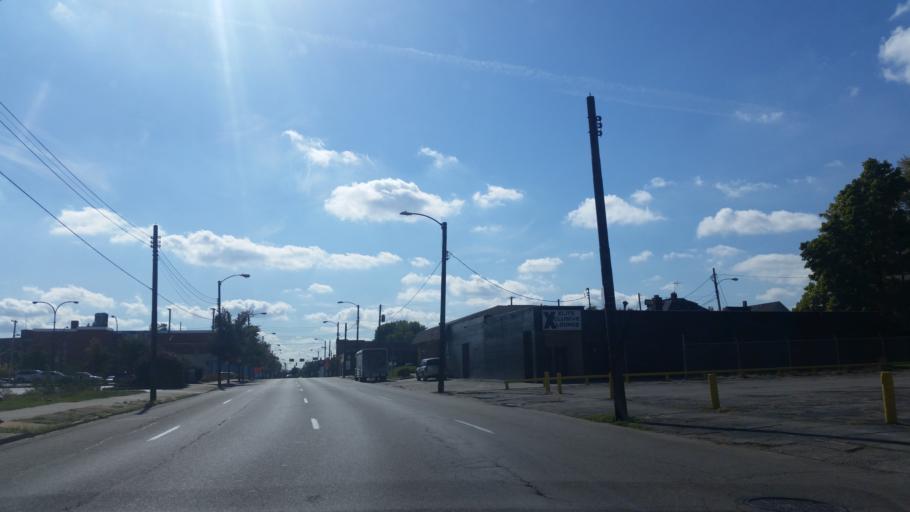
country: US
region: Ohio
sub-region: Summit County
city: Akron
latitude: 41.0587
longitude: -81.5289
